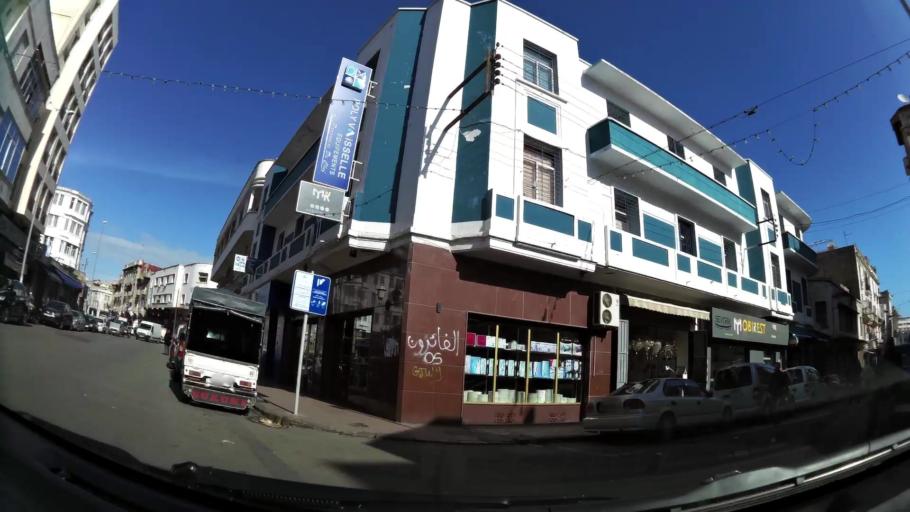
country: MA
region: Grand Casablanca
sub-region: Casablanca
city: Casablanca
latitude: 33.5934
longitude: -7.6129
